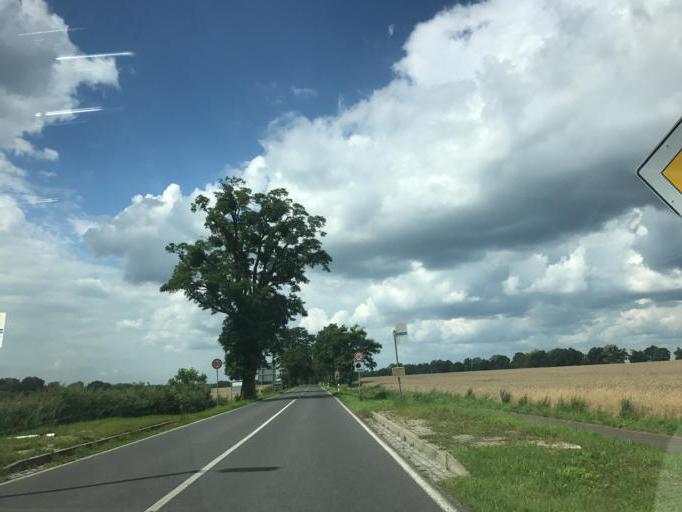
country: DE
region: Brandenburg
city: Grosswoltersdorf
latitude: 53.0858
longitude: 13.0725
